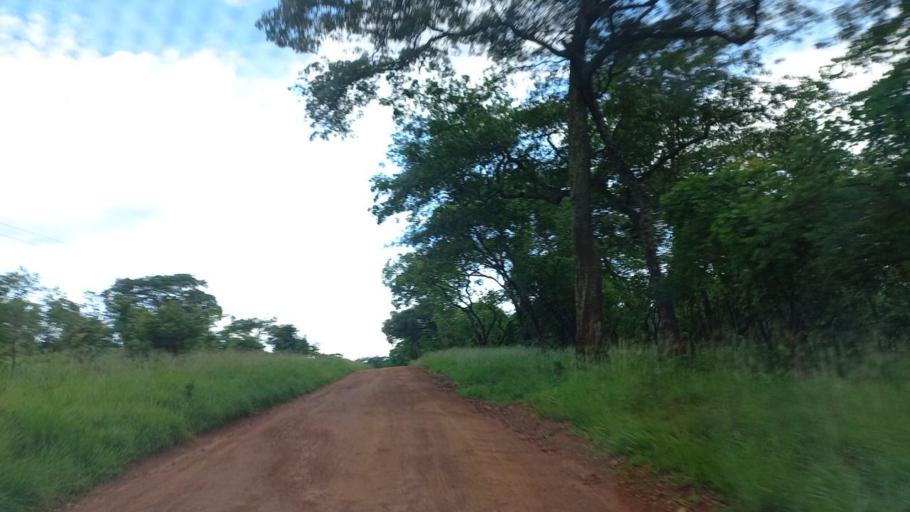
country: ZM
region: North-Western
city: Mwinilunga
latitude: -11.7864
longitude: 24.3732
